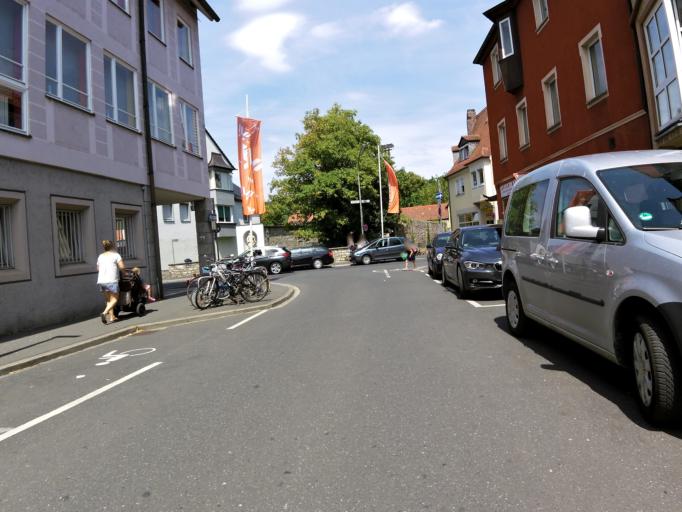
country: DE
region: Bavaria
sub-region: Regierungsbezirk Unterfranken
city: Wuerzburg
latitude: 49.7641
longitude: 9.9493
